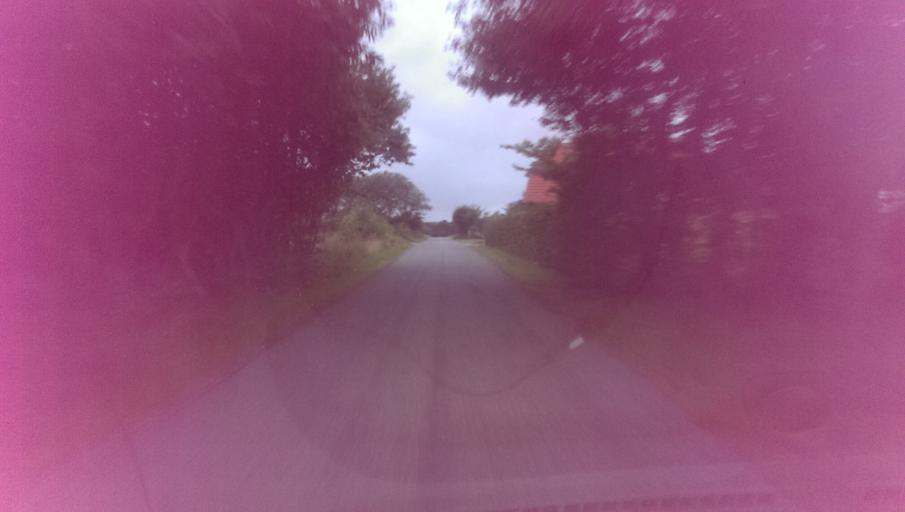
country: DK
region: South Denmark
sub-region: Esbjerg Kommune
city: Tjaereborg
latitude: 55.4806
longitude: 8.5182
